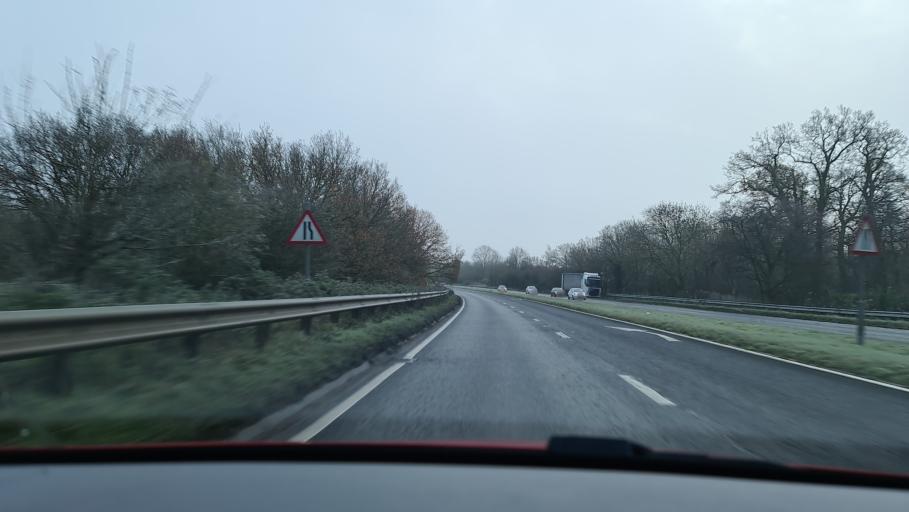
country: GB
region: England
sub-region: Buckinghamshire
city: Seer Green
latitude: 51.6000
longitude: -0.6208
